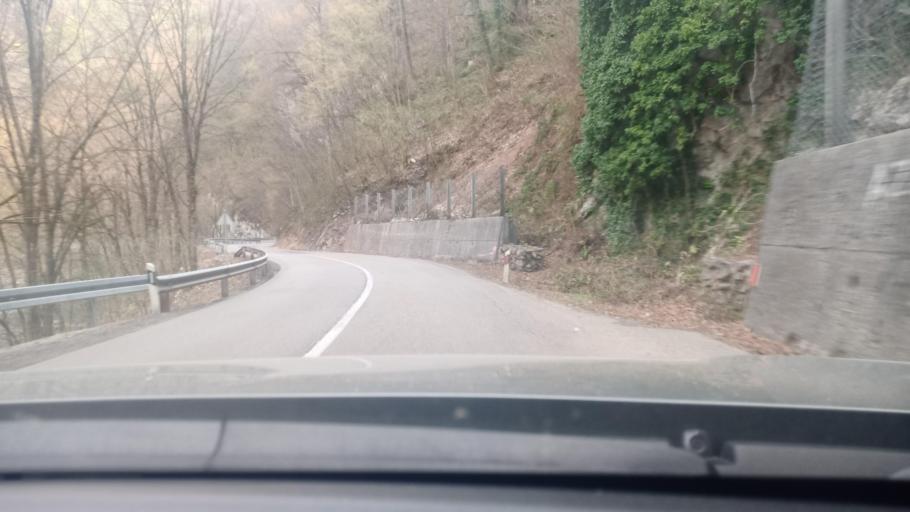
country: BA
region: Federation of Bosnia and Herzegovina
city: Bosanska Krupa
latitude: 44.8650
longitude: 16.0908
